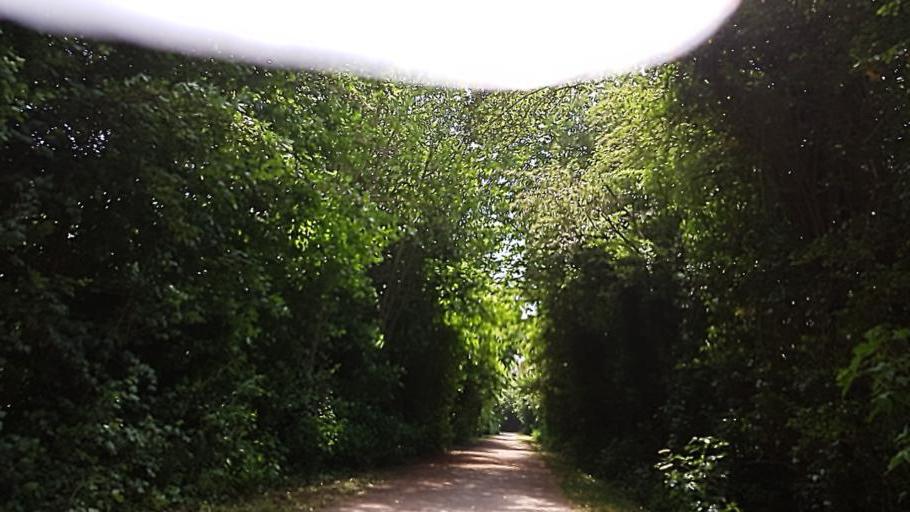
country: FR
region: Nord-Pas-de-Calais
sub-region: Departement du Nord
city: Vieux-Conde
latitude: 50.4747
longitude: 3.5717
